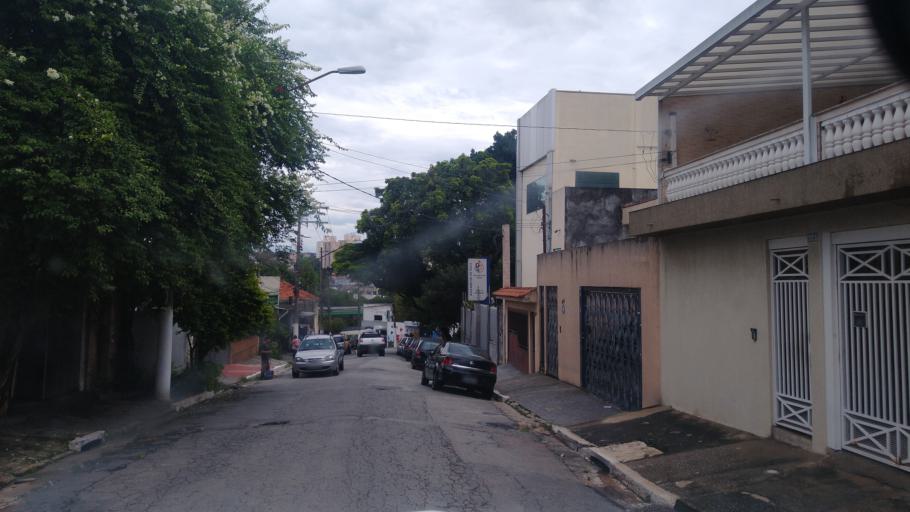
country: BR
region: Sao Paulo
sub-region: Guarulhos
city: Guarulhos
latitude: -23.5162
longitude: -46.5299
